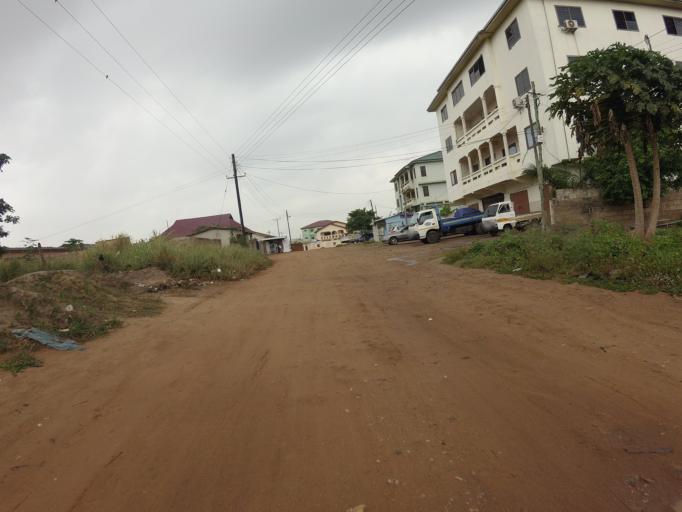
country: GH
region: Greater Accra
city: Dome
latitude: 5.6318
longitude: -0.2314
